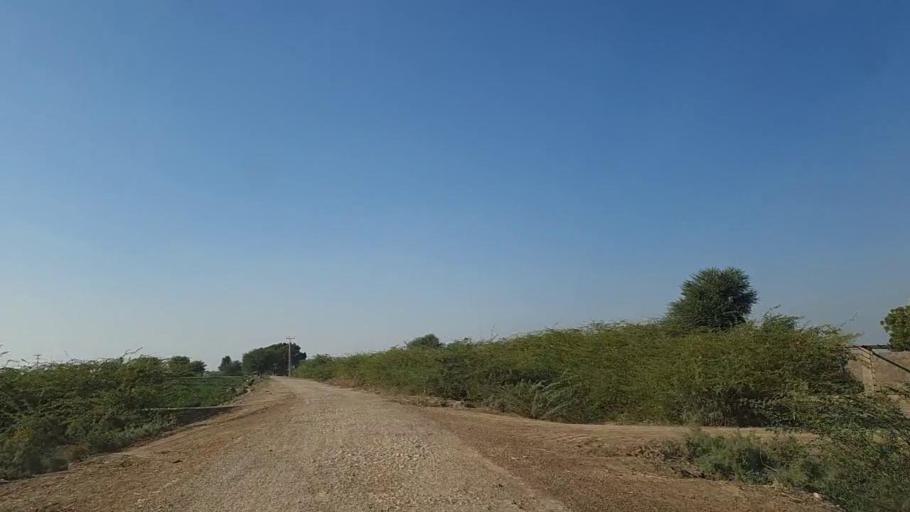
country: PK
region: Sindh
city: Samaro
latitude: 25.3628
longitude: 69.3867
